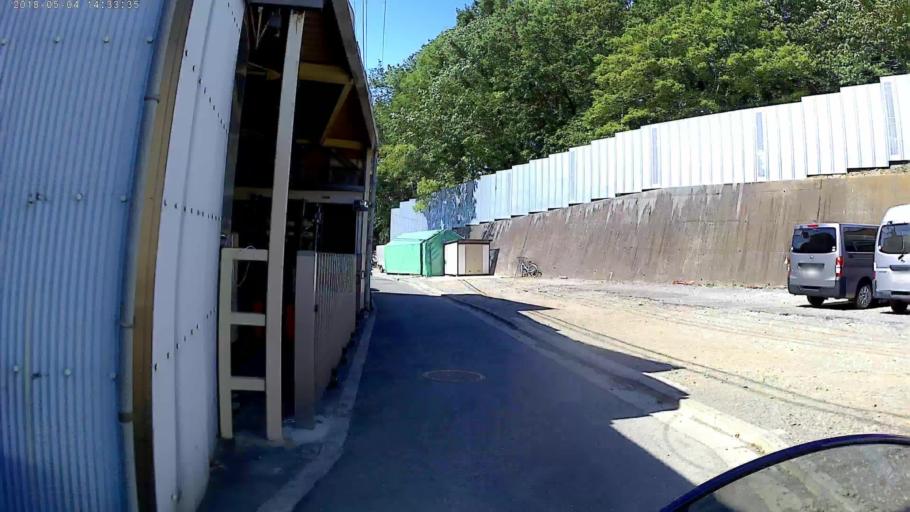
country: JP
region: Kanagawa
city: Yokohama
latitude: 35.4898
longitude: 139.5993
